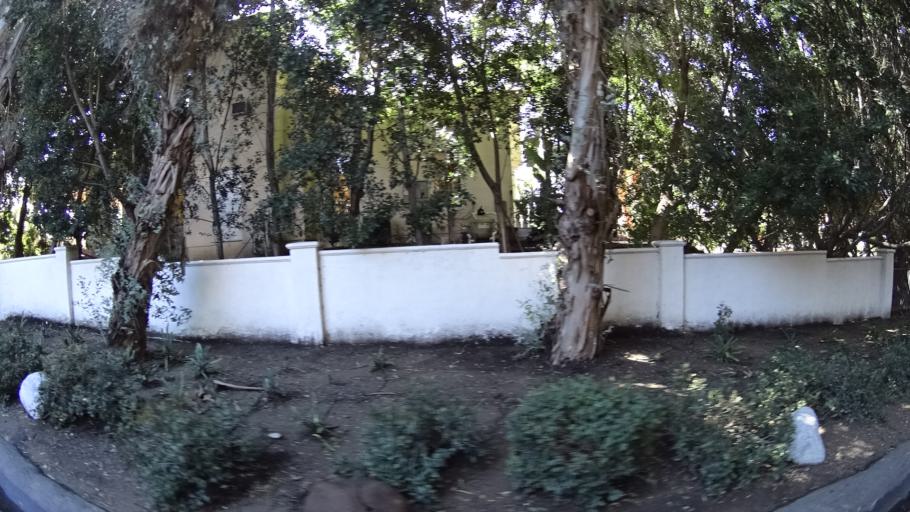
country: US
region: California
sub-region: Orange County
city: Villa Park
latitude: 33.8491
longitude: -117.8131
